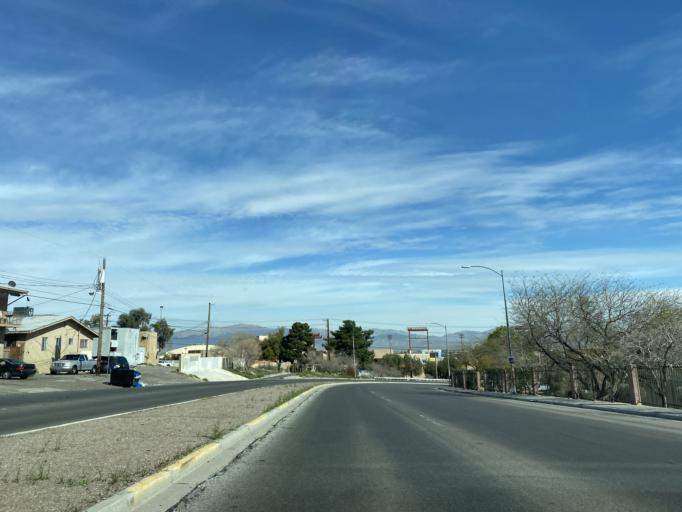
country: US
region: Nevada
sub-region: Clark County
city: Las Vegas
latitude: 36.1764
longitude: -115.1306
